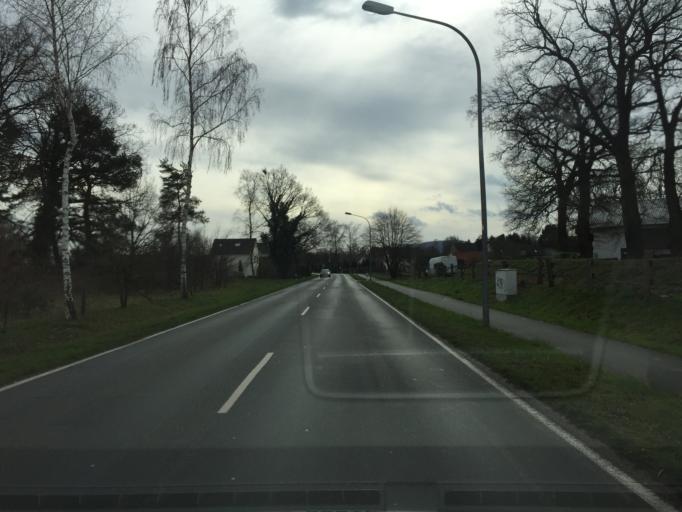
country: DE
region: North Rhine-Westphalia
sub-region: Regierungsbezirk Detmold
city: Lage
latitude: 51.9621
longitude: 8.8056
